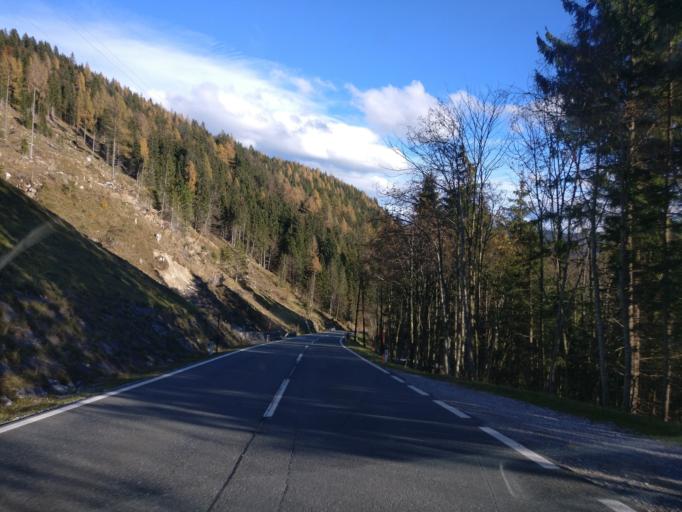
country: AT
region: Salzburg
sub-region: Politischer Bezirk Sankt Johann im Pongau
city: Muhlbach am Hochkonig
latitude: 47.3913
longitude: 13.0952
